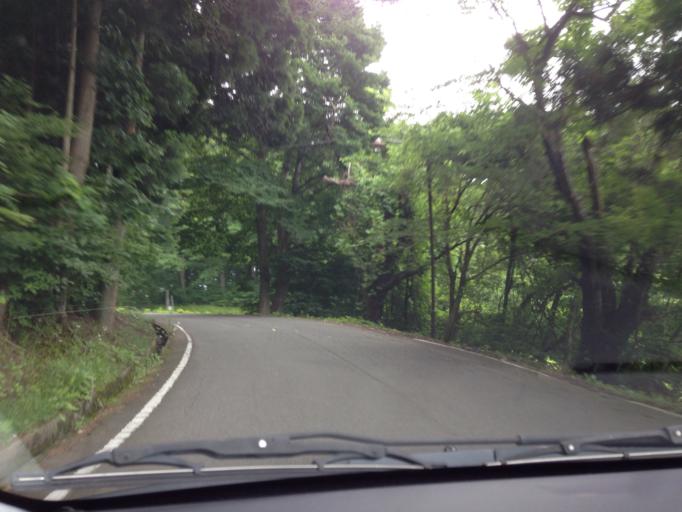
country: JP
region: Fukushima
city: Inawashiro
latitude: 37.5206
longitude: 140.0434
